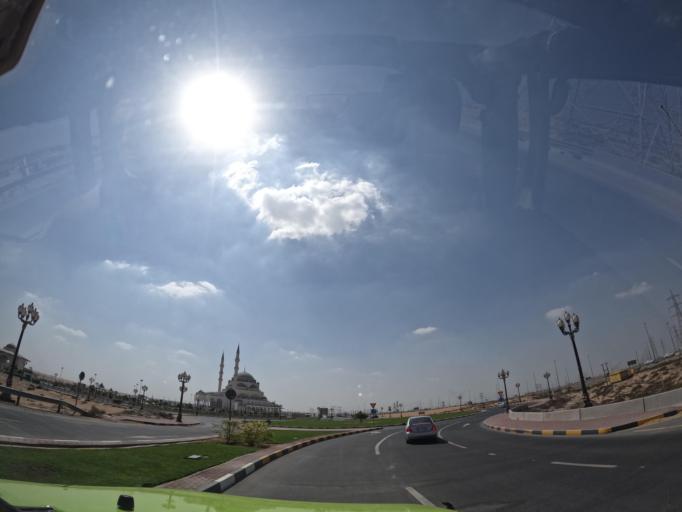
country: AE
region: Ash Shariqah
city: Sharjah
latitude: 25.2442
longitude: 55.5708
